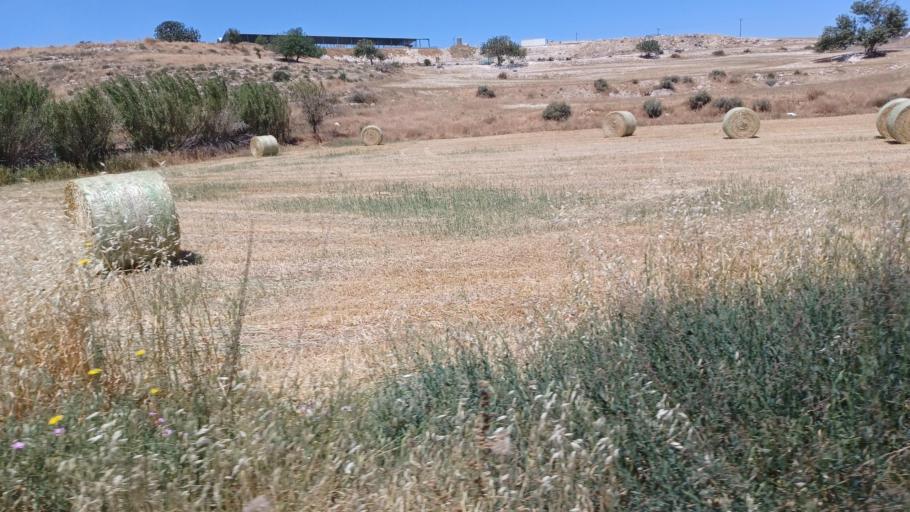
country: CY
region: Larnaka
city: Athienou
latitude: 35.0350
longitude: 33.5426
